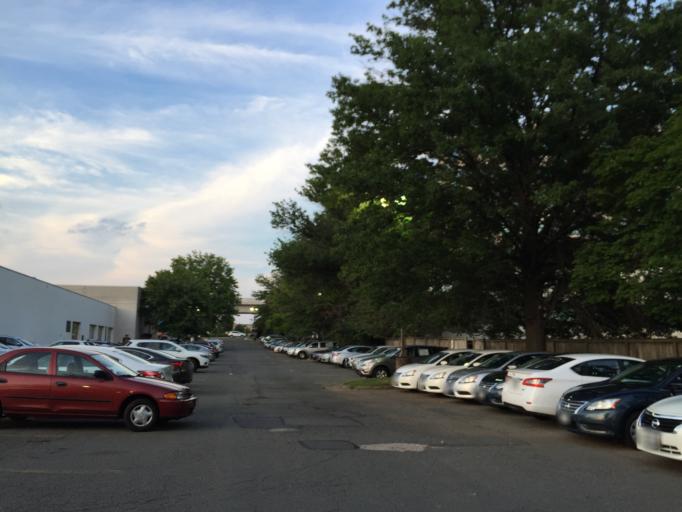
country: US
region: Virginia
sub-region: Fairfax County
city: Tysons Corner
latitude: 38.9261
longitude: -77.2414
